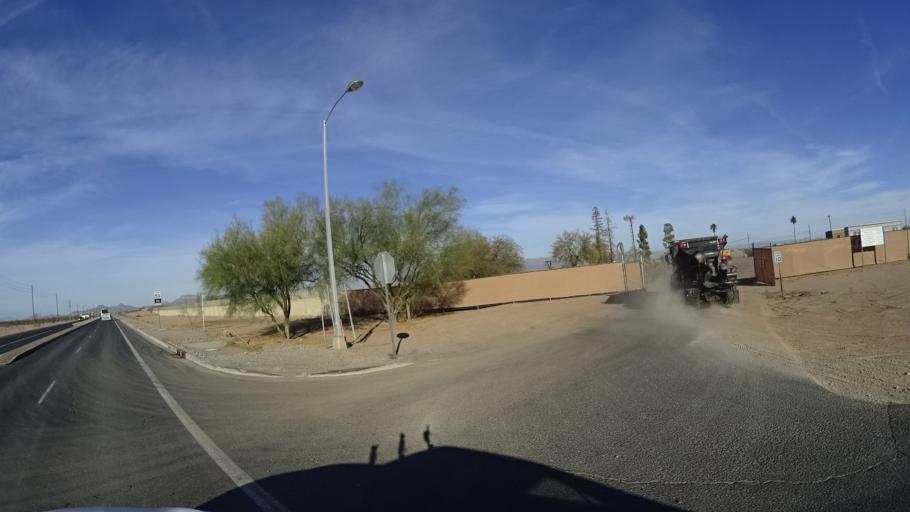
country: US
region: Arizona
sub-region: Maricopa County
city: Queen Creek
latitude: 33.3290
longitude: -111.6356
